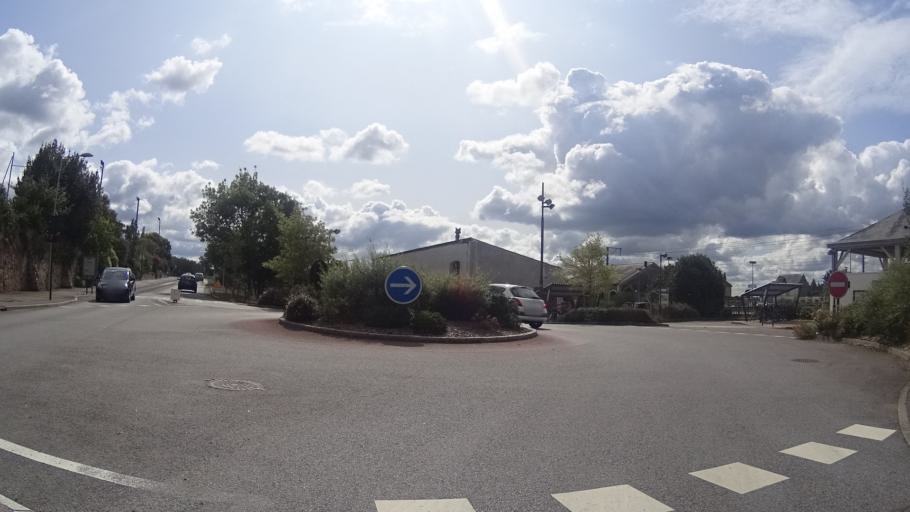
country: FR
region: Pays de la Loire
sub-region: Departement de la Loire-Atlantique
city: Savenay
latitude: 47.3588
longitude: -1.9506
